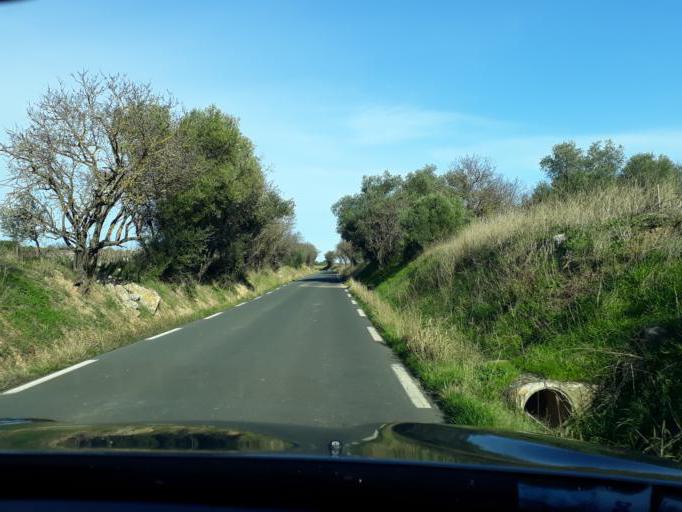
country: FR
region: Languedoc-Roussillon
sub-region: Departement de l'Herault
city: Castelnau-de-Guers
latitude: 43.4263
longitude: 3.4333
